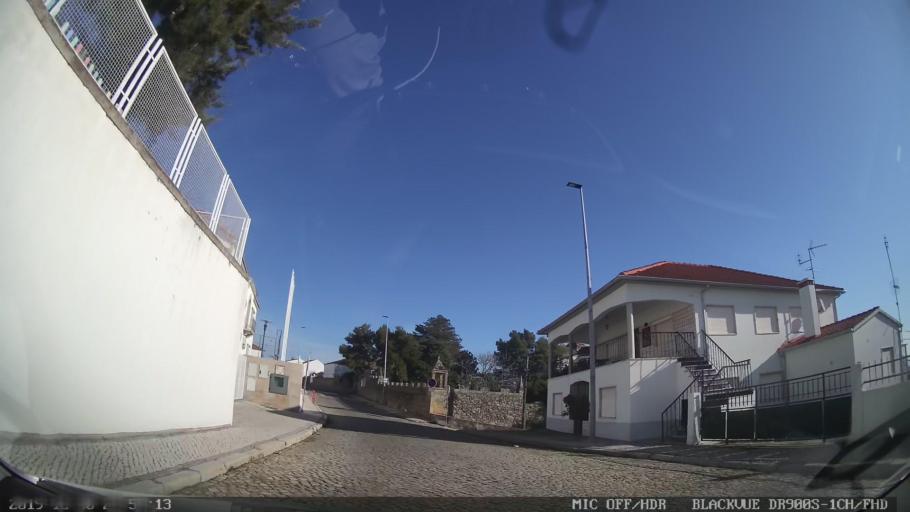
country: PT
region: Castelo Branco
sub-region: Idanha-A-Nova
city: Idanha-a-Nova
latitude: 39.9235
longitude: -7.2393
